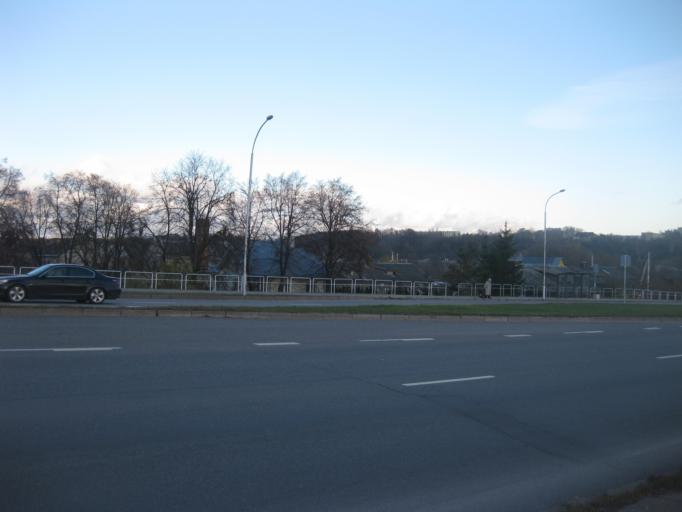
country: LT
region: Kauno apskritis
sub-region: Kaunas
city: Silainiai
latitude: 54.9253
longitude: 23.9051
